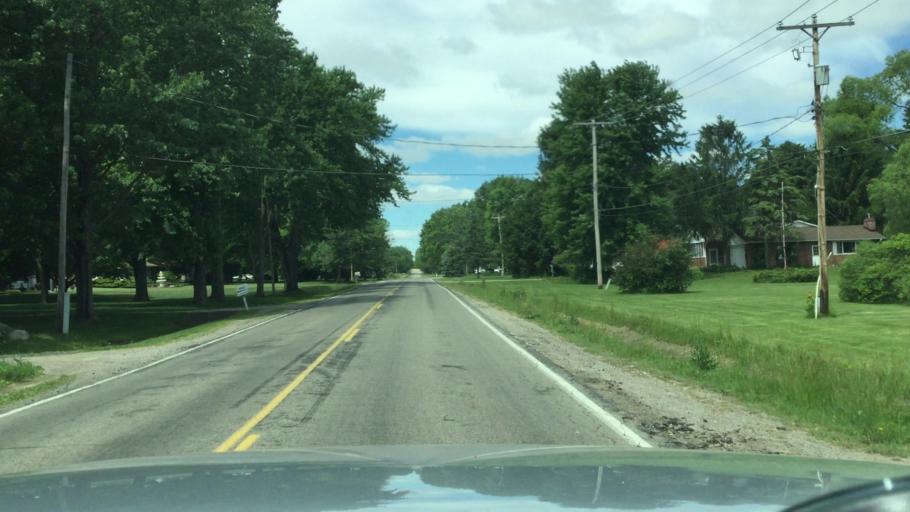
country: US
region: Michigan
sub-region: Genesee County
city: Clio
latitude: 43.1920
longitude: -83.7547
